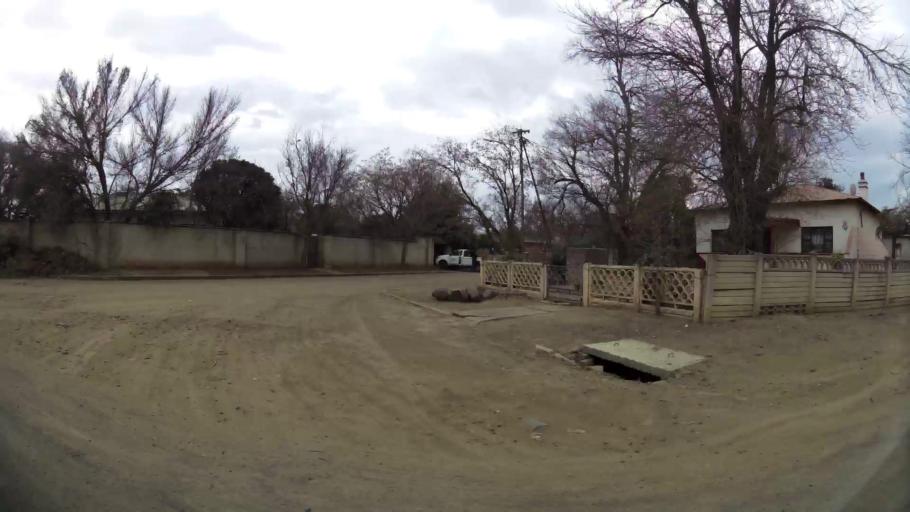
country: ZA
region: Orange Free State
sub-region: Fezile Dabi District Municipality
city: Kroonstad
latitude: -27.6753
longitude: 27.2315
